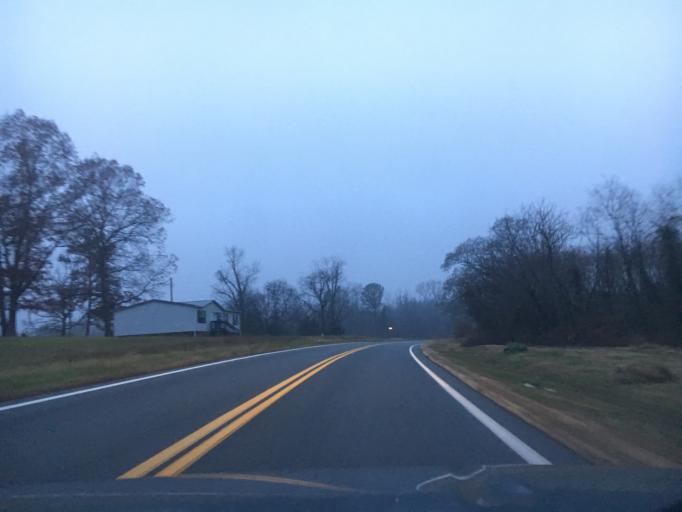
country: US
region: Virginia
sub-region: Halifax County
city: Mountain Road
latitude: 36.6839
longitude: -78.9942
